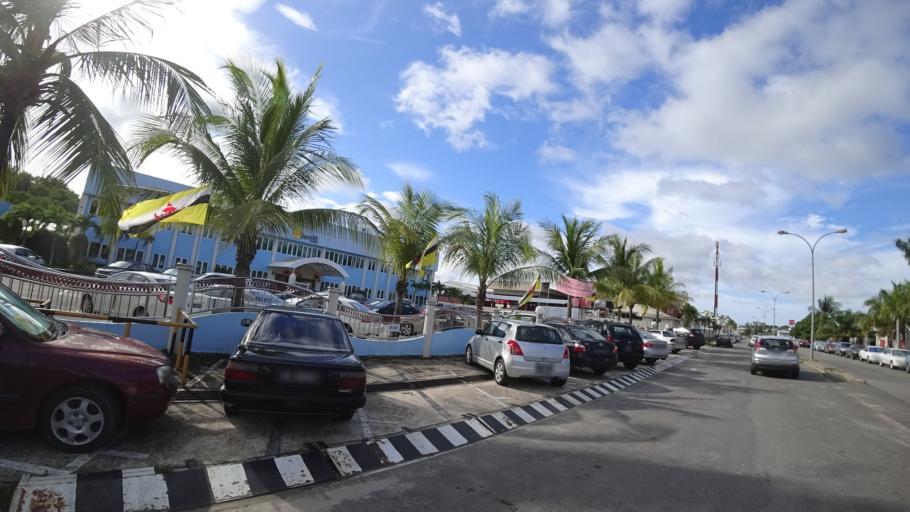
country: BN
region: Brunei and Muara
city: Bandar Seri Begawan
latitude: 4.8913
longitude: 114.9049
